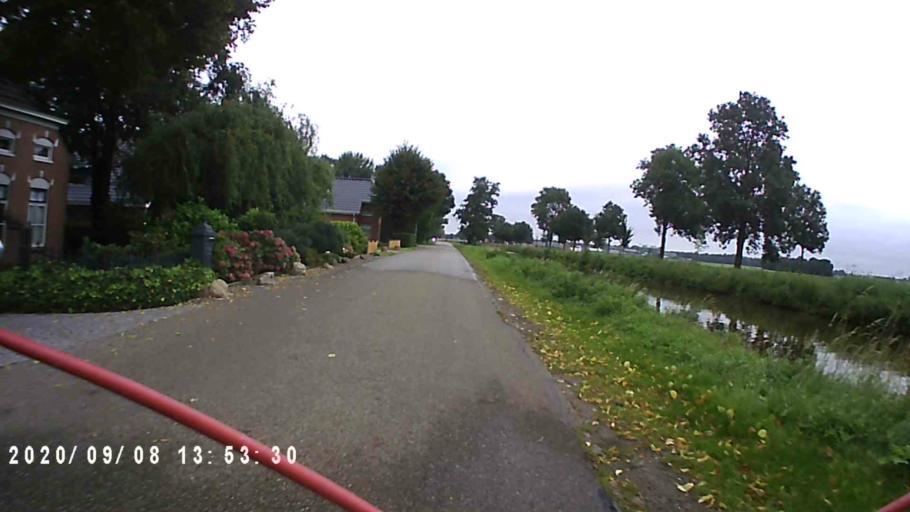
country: NL
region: Groningen
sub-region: Gemeente Veendam
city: Veendam
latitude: 53.1491
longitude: 6.8654
